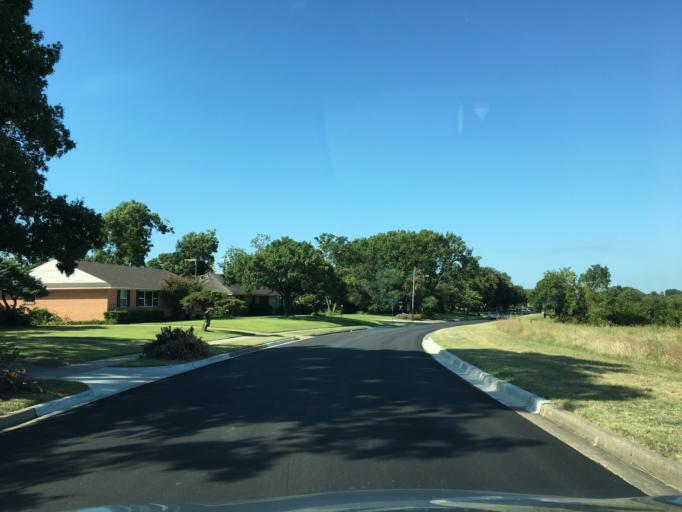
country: US
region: Texas
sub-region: Dallas County
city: Highland Park
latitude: 32.8577
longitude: -96.7104
